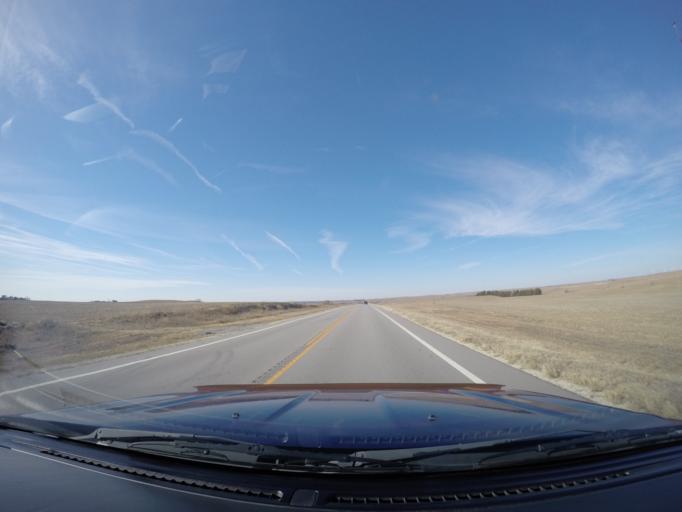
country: US
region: Kansas
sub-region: Cloud County
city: Concordia
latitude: 39.3646
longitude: -97.5290
